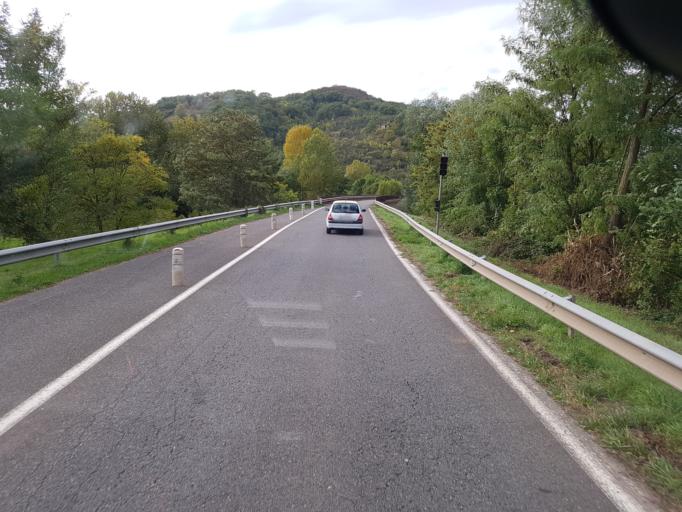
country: FR
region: Midi-Pyrenees
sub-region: Departement de l'Aveyron
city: Saint-Affrique
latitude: 43.9514
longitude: 2.8414
